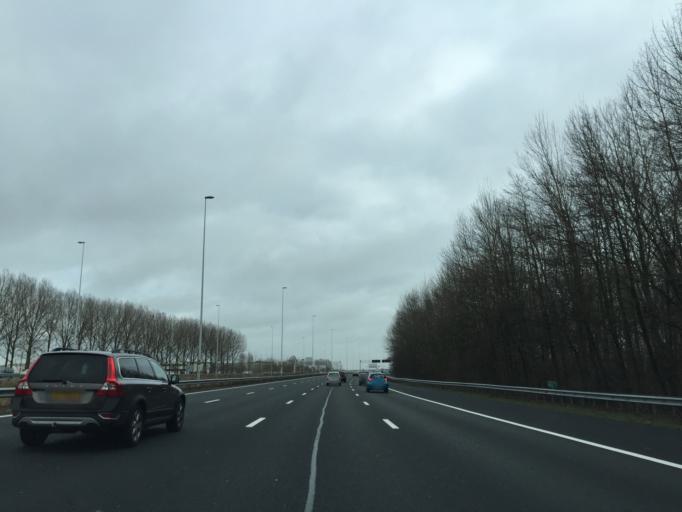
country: NL
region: South Holland
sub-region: Bodegraven-Reeuwijk
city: Bodegraven
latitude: 52.0669
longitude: 4.7514
